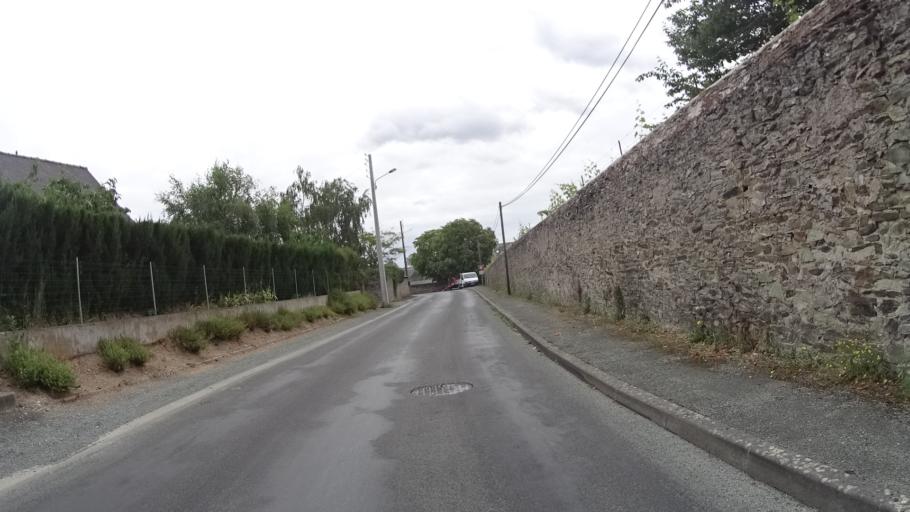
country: FR
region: Pays de la Loire
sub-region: Departement de Maine-et-Loire
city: Savennieres
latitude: 47.3836
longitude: -0.6621
